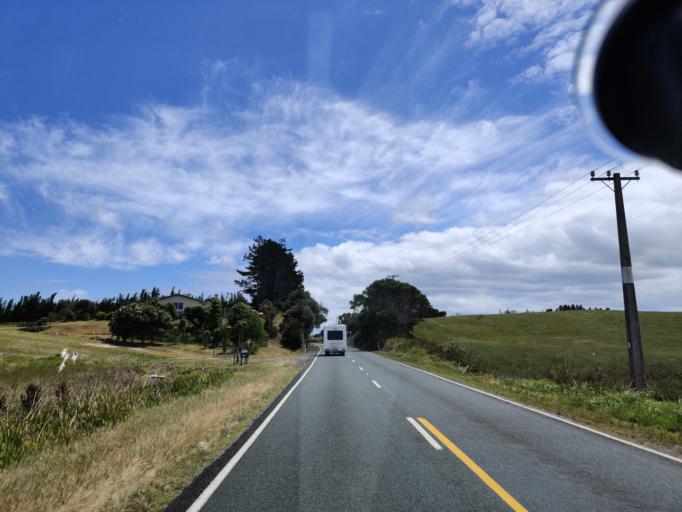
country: NZ
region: Northland
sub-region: Far North District
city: Kaitaia
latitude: -34.7533
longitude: 173.0620
